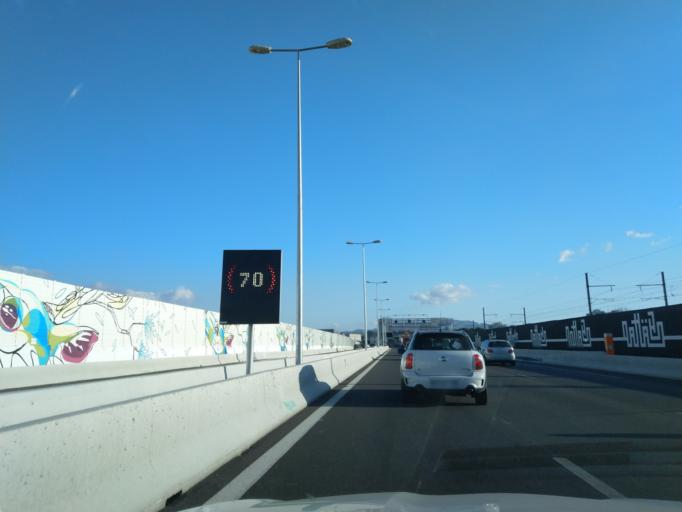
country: FR
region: Provence-Alpes-Cote d'Azur
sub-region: Departement des Bouches-du-Rhone
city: Marseille 14
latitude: 43.3370
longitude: 5.3793
